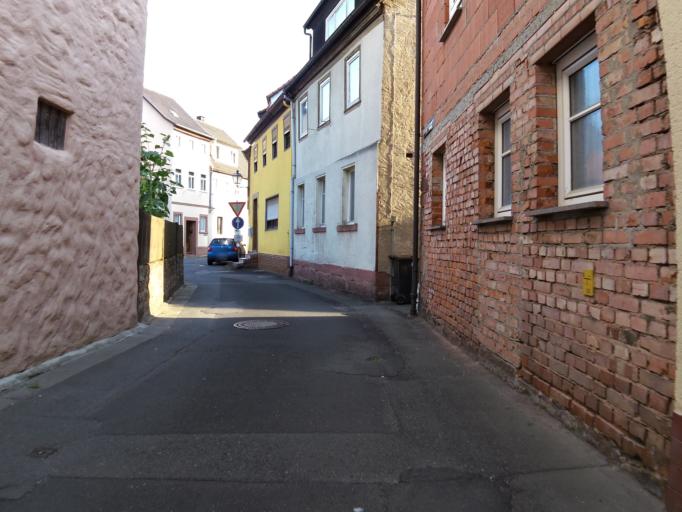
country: DE
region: Bavaria
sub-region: Regierungsbezirk Unterfranken
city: Weilbach
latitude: 49.6452
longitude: 9.2169
